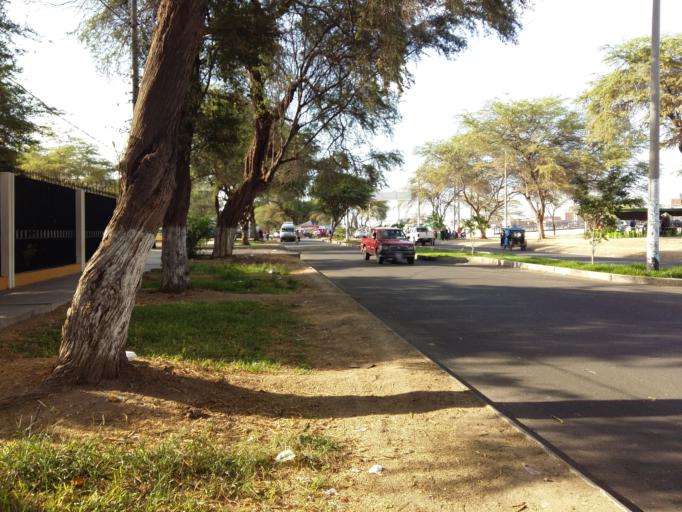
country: PE
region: Piura
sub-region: Provincia de Piura
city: Piura
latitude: -5.1871
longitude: -80.6236
